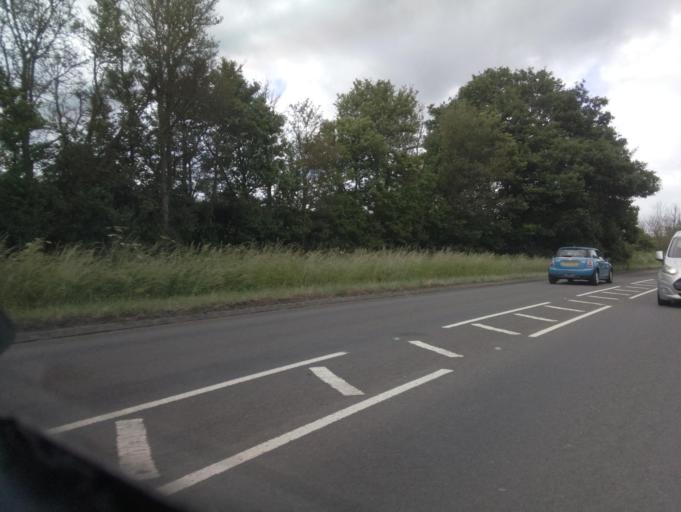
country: GB
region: England
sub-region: Dudley
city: Kingswinford
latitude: 52.4475
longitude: -2.2102
